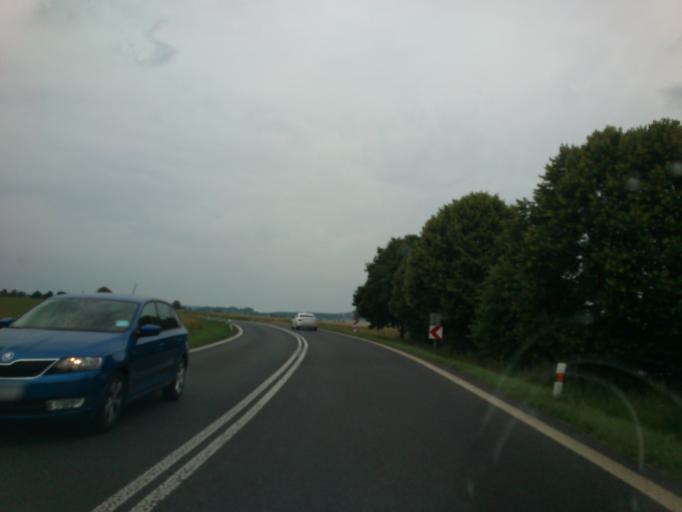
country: CZ
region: Central Bohemia
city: Bela pod Bezdezem
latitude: 50.5139
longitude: 14.7752
